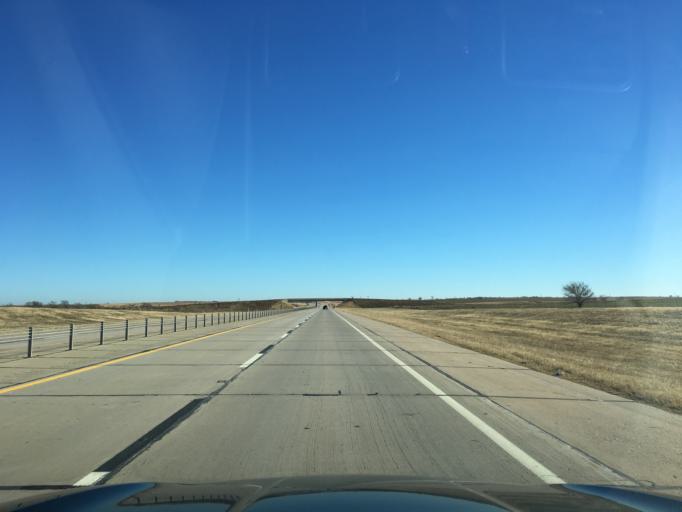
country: US
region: Oklahoma
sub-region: Noble County
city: Perry
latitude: 36.3979
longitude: -97.2346
